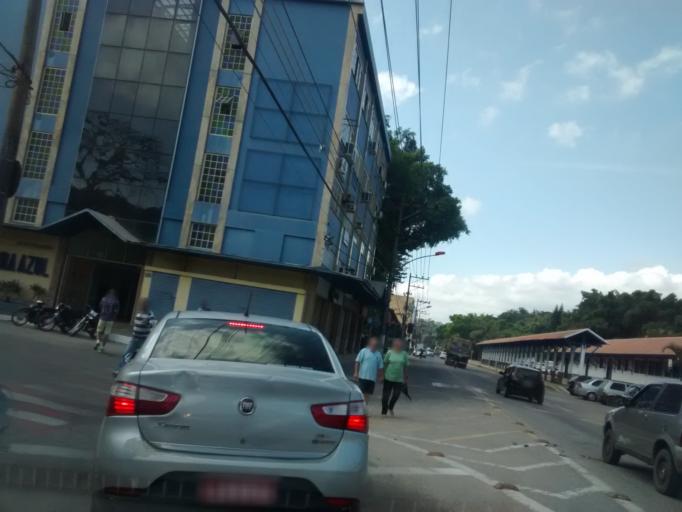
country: BR
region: Rio de Janeiro
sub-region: Miguel Pereira
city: Miguel Pereira
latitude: -22.4548
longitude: -43.4704
